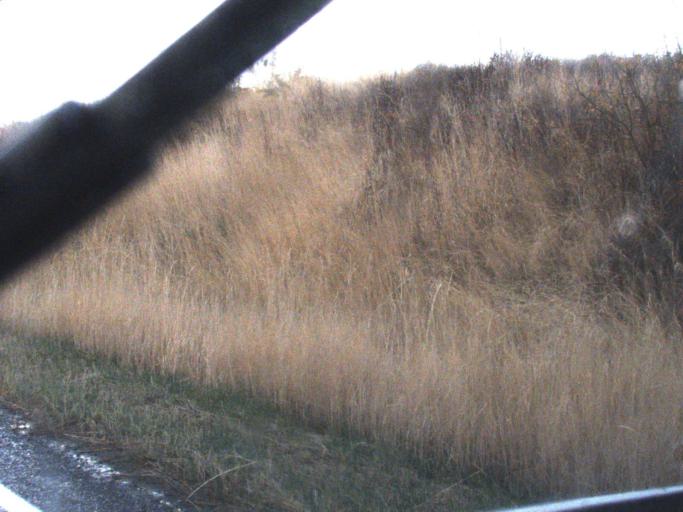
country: US
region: Washington
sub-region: Stevens County
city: Kettle Falls
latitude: 48.4763
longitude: -118.1692
